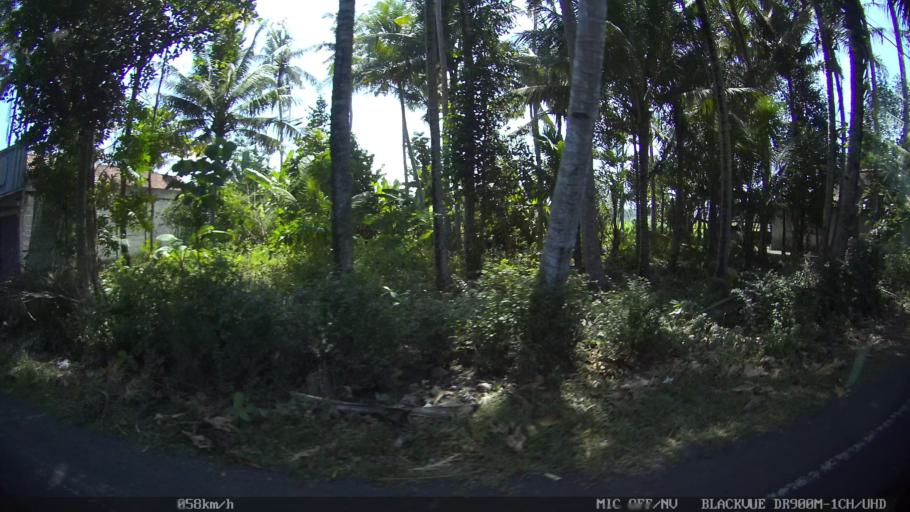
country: ID
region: Daerah Istimewa Yogyakarta
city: Srandakan
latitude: -7.9164
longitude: 110.1032
